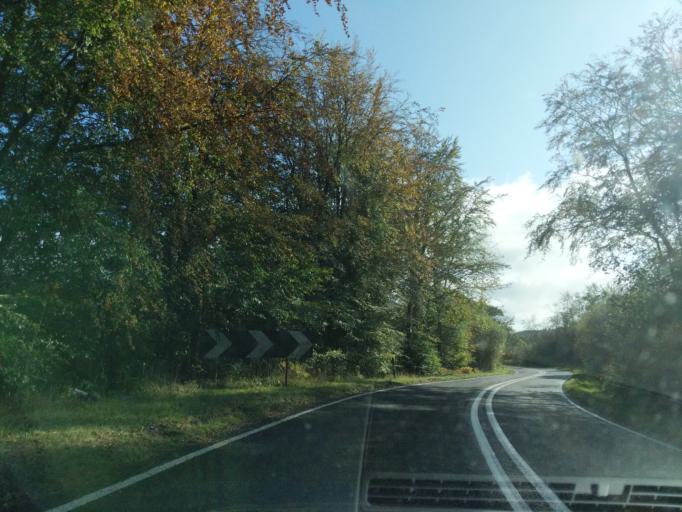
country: GB
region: Scotland
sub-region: Dumfries and Galloway
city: Moffat
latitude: 55.3487
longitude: -3.4624
